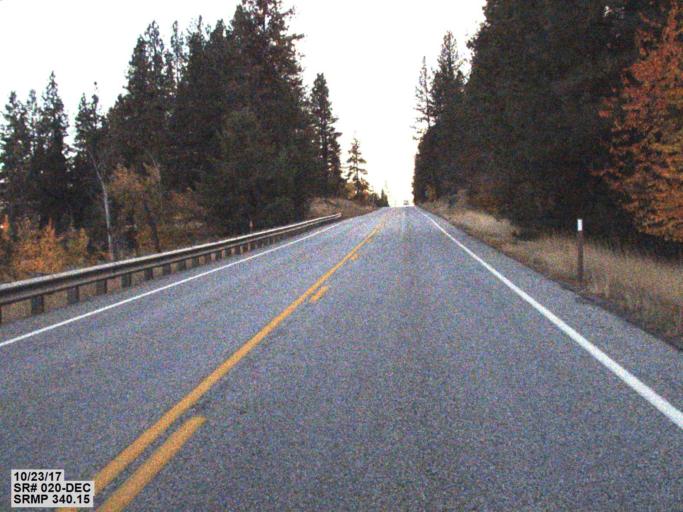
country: US
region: Washington
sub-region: Stevens County
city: Kettle Falls
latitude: 48.6042
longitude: -118.1394
